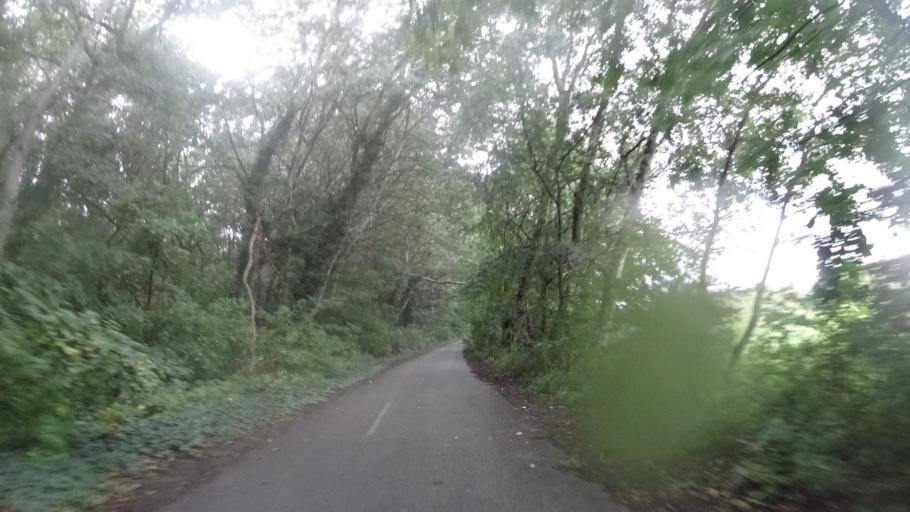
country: HU
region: Komarom-Esztergom
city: Labatlan
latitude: 47.7562
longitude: 18.5003
